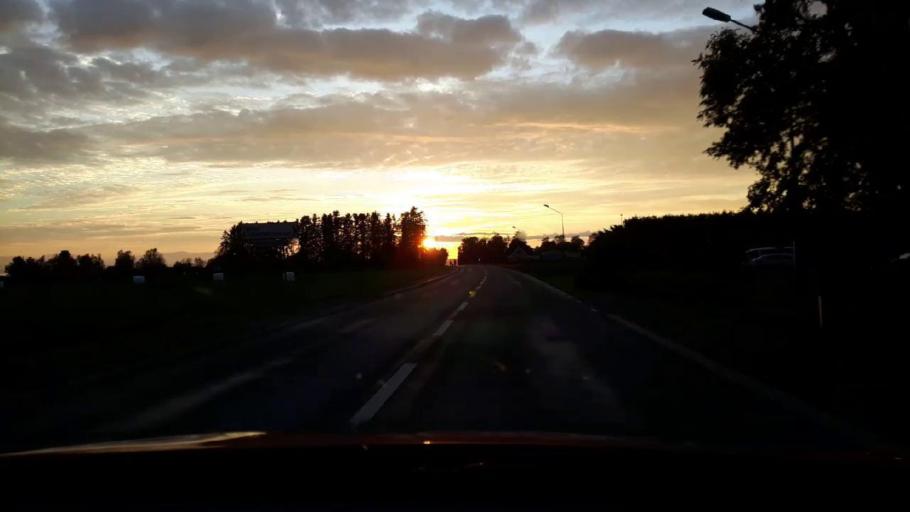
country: SE
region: Jaemtland
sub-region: OEstersunds Kommun
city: Ostersund
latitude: 63.2481
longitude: 14.5603
